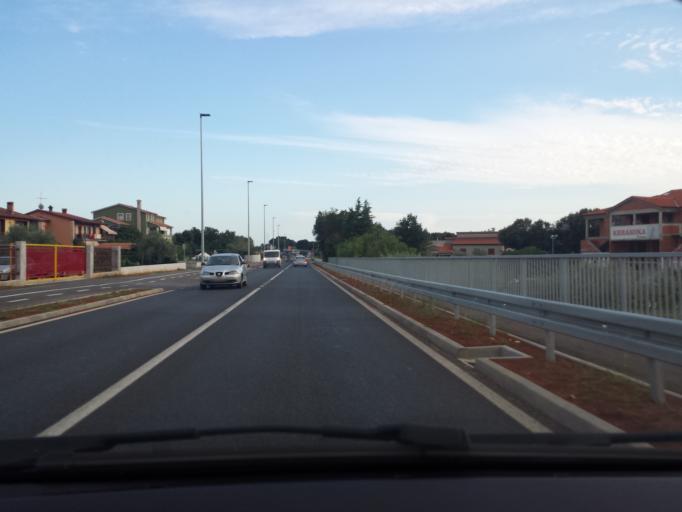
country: HR
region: Istarska
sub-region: Grad Pula
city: Pula
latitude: 44.9017
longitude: 13.8456
